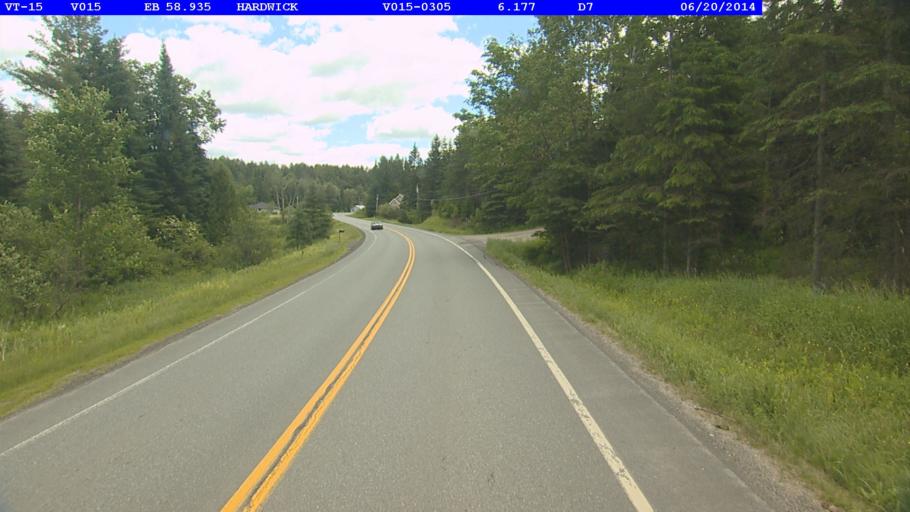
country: US
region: Vermont
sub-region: Caledonia County
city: Hardwick
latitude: 44.4949
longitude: -72.3183
